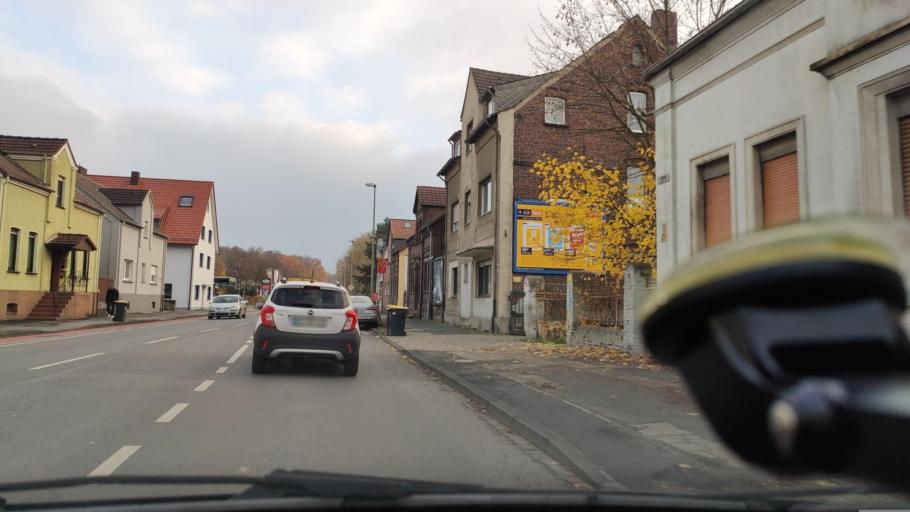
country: DE
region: North Rhine-Westphalia
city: Lunen
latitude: 51.5932
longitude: 7.5348
